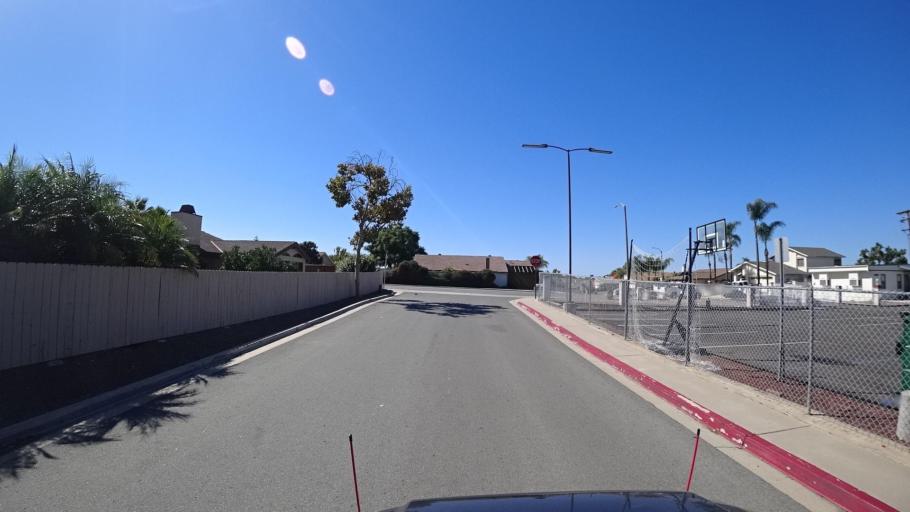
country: US
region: California
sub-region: San Diego County
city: La Presa
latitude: 32.6977
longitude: -117.0154
